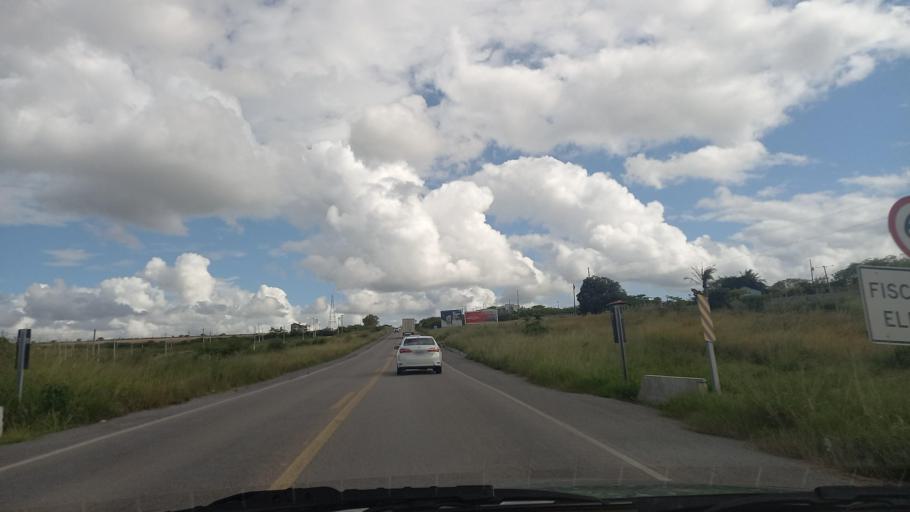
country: BR
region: Pernambuco
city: Garanhuns
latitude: -8.8276
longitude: -36.4514
